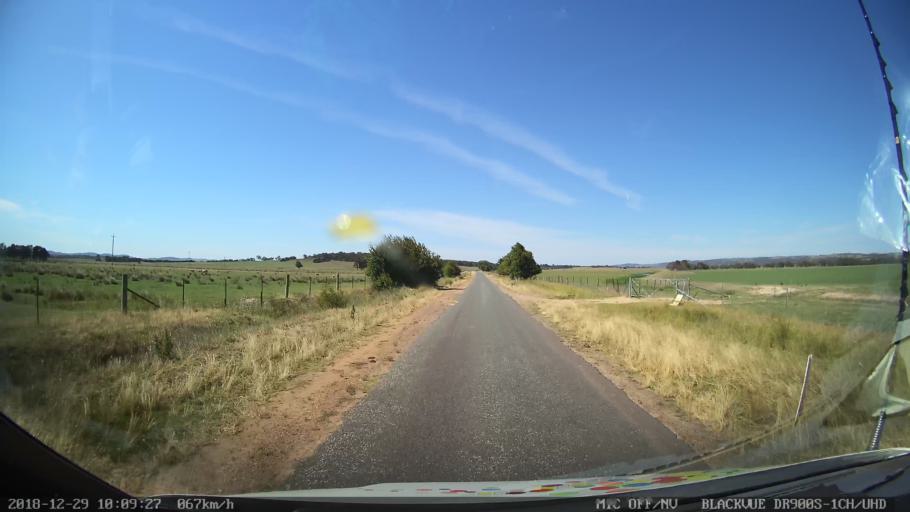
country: AU
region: New South Wales
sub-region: Yass Valley
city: Gundaroo
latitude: -34.8658
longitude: 149.4599
